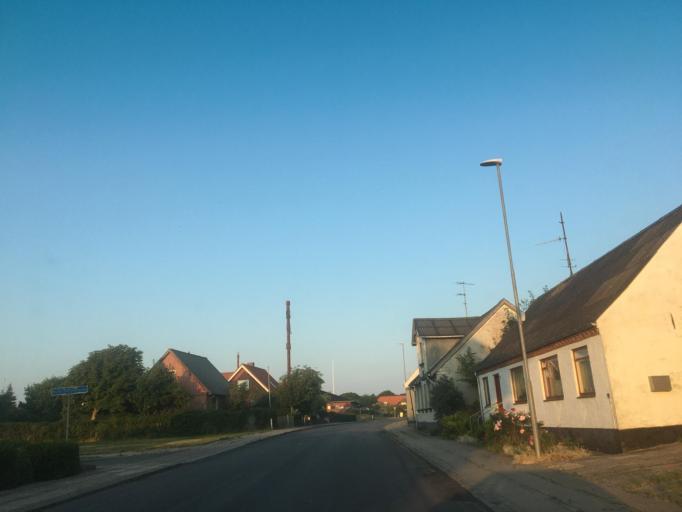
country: DK
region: North Denmark
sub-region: Thisted Kommune
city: Hurup
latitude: 56.7634
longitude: 8.3138
